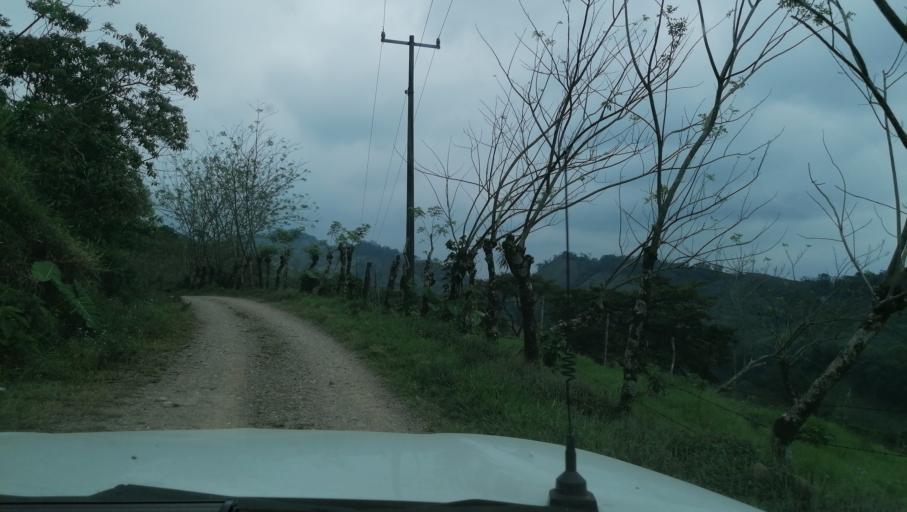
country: MX
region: Chiapas
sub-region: Francisco Leon
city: San Miguel la Sardina
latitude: 17.3391
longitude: -93.3136
